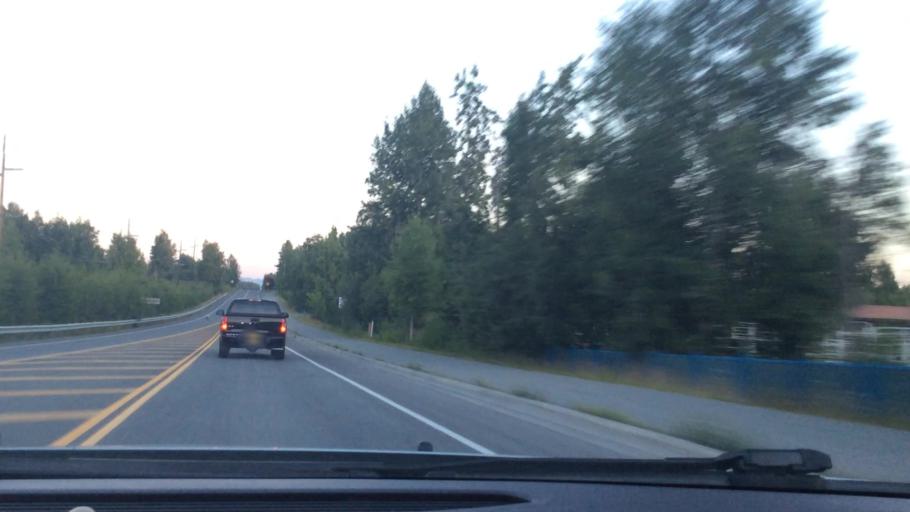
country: US
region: Alaska
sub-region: Anchorage Municipality
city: Anchorage
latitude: 61.1510
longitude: -149.8043
